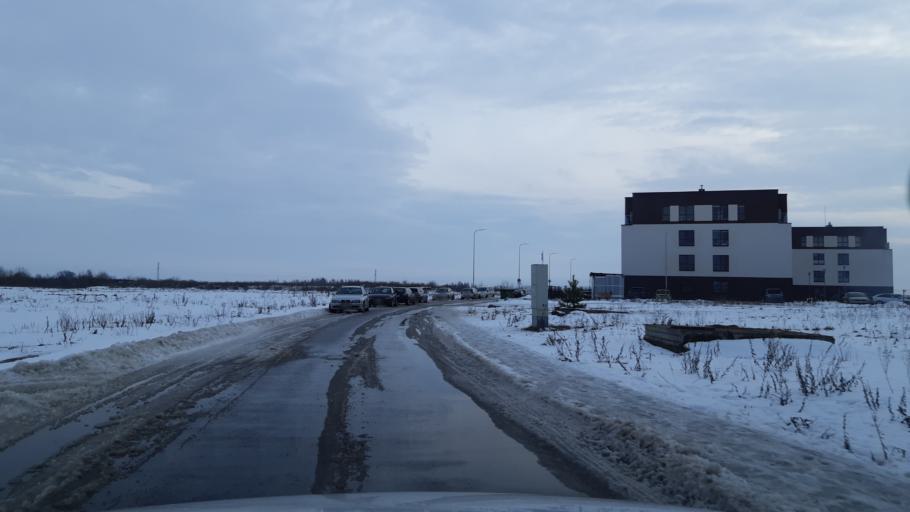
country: LT
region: Kauno apskritis
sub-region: Kauno rajonas
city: Garliava
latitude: 54.8382
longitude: 23.9057
